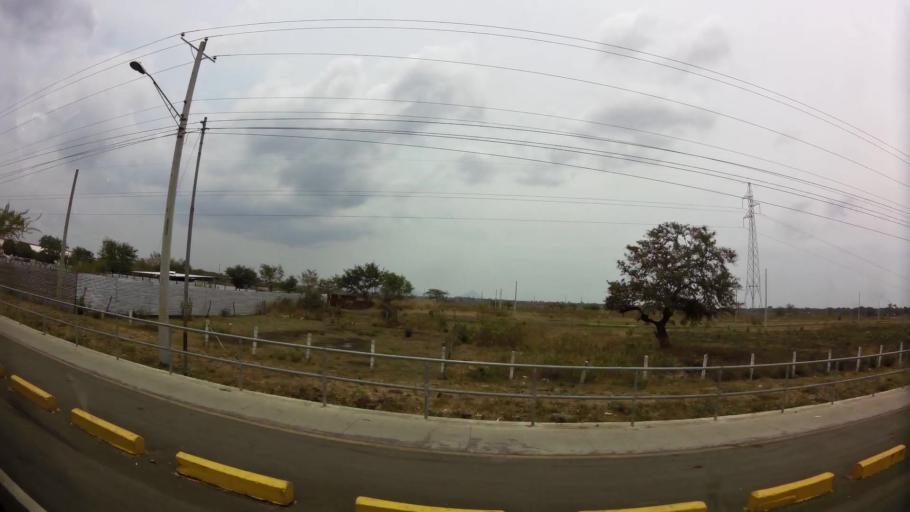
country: NI
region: Leon
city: Leon
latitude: 12.4415
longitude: -86.8632
